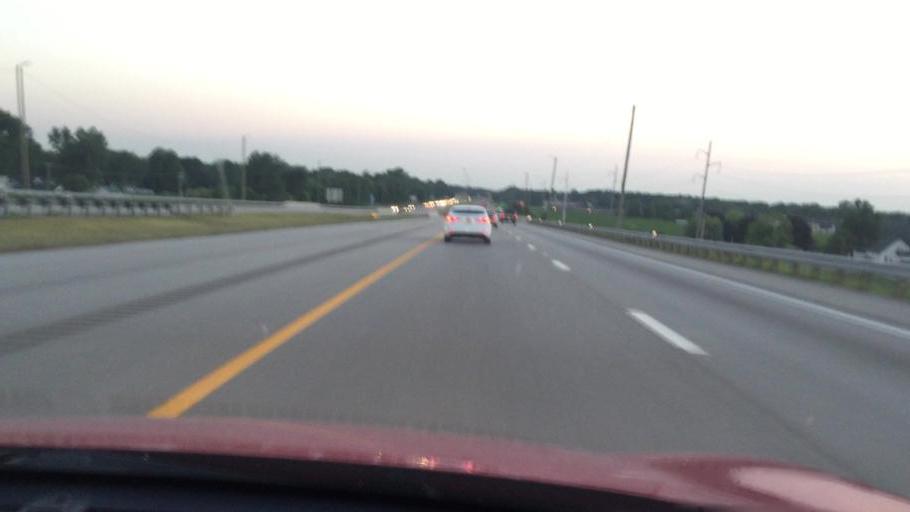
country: US
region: Ohio
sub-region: Lucas County
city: Holland
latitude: 41.6224
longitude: -83.6921
